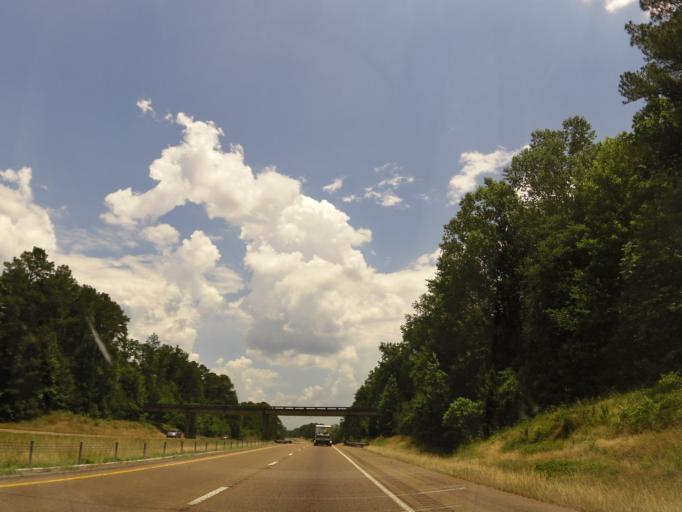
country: US
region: Mississippi
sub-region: Lauderdale County
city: Marion
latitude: 32.3883
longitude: -88.6077
